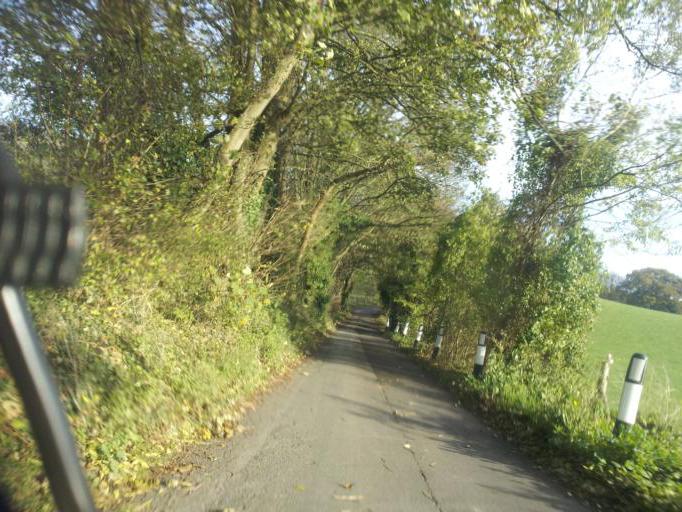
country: GB
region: England
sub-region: Kent
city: Boxley
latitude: 51.3034
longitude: 0.5547
